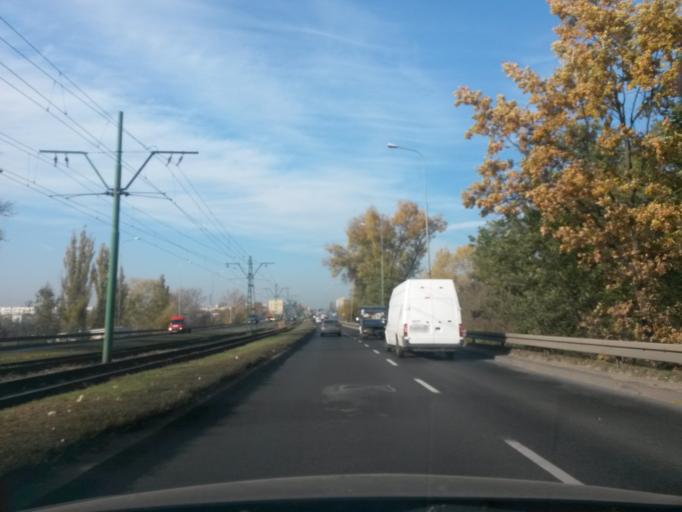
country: PL
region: Greater Poland Voivodeship
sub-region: Poznan
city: Poznan
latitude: 52.3824
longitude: 16.9324
